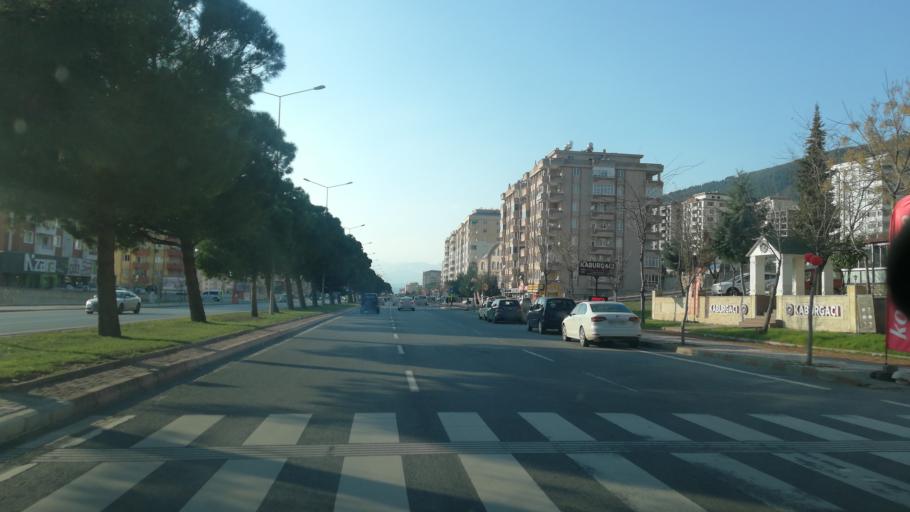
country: TR
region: Kahramanmaras
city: Kahramanmaras
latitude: 37.5941
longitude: 36.8563
